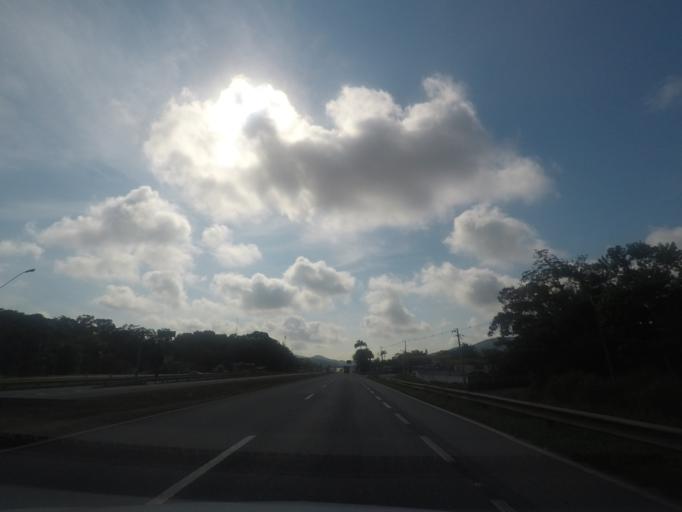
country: BR
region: Parana
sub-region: Antonina
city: Antonina
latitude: -25.5521
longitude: -48.7989
